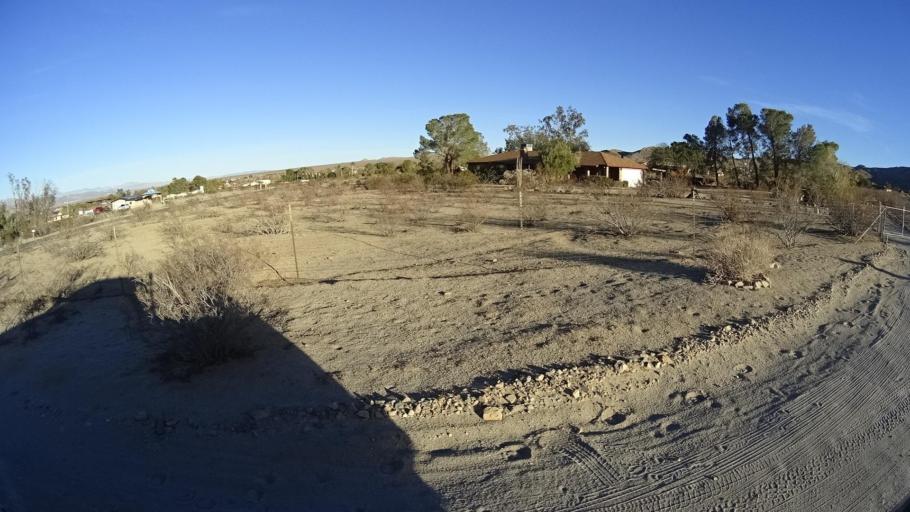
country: US
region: California
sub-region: Kern County
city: Ridgecrest
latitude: 35.5859
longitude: -117.6614
